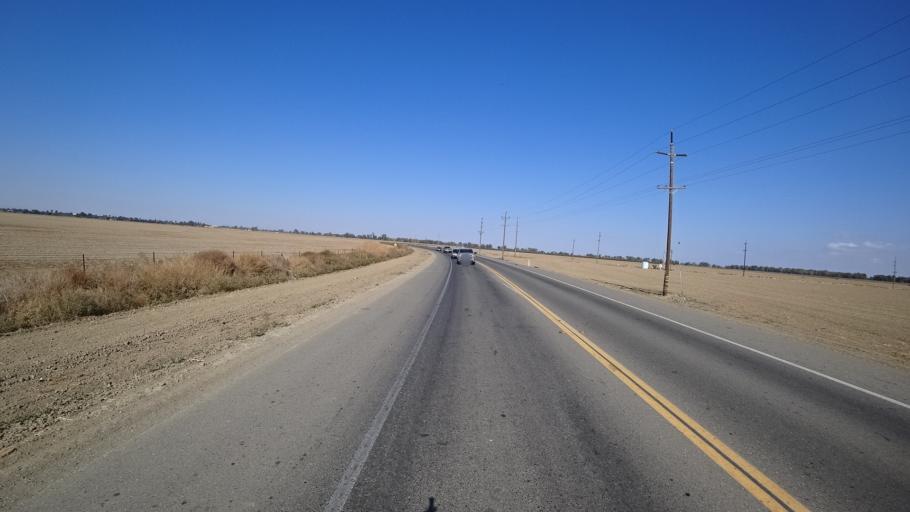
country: US
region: California
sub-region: Yolo County
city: Woodland
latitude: 38.7115
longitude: -121.7282
